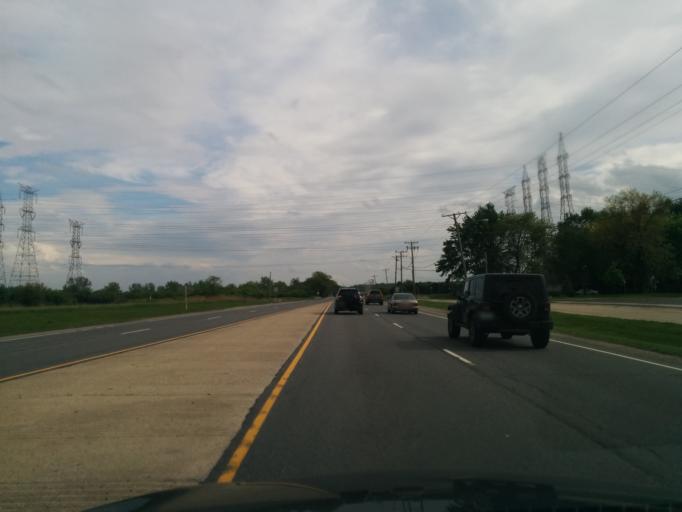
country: US
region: Illinois
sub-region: Will County
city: Romeoville
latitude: 41.6340
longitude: -88.0805
